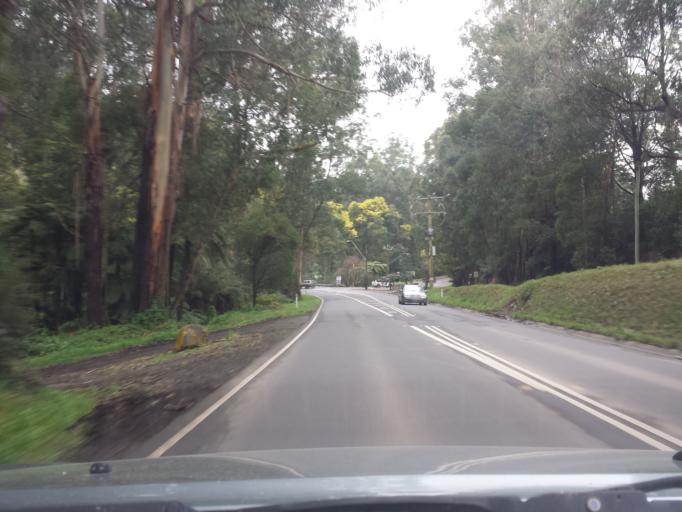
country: AU
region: Victoria
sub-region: Yarra Ranges
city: Monbulk
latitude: -37.8802
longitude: 145.3960
